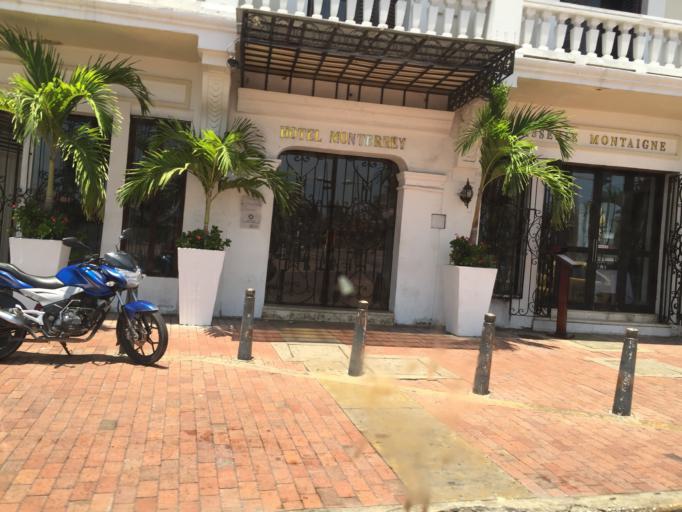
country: CO
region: Bolivar
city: Cartagena
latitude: 10.4218
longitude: -75.5477
